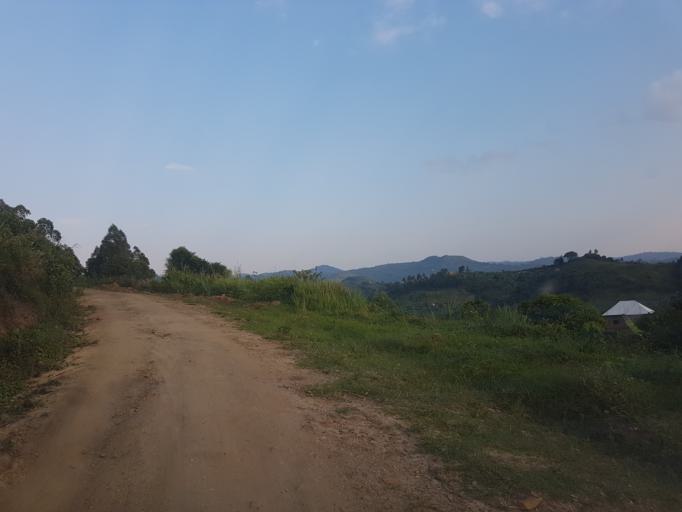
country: UG
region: Western Region
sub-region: Mitoma District
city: Mitoma
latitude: -0.6818
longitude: 29.9094
